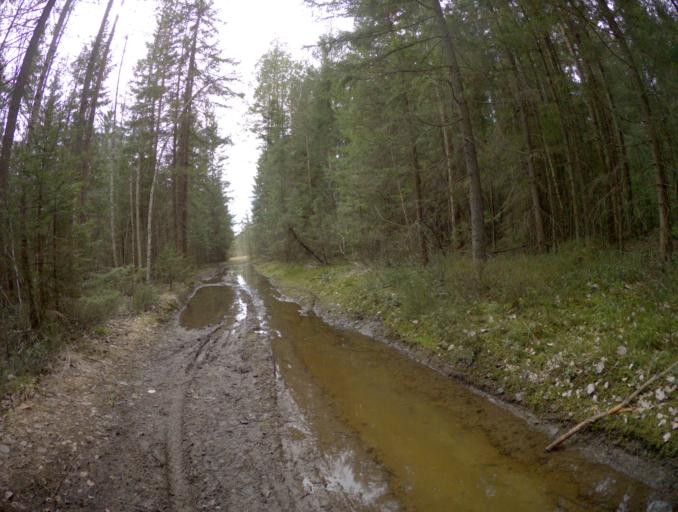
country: RU
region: Vladimir
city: Raduzhnyy
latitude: 55.9472
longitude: 40.2646
